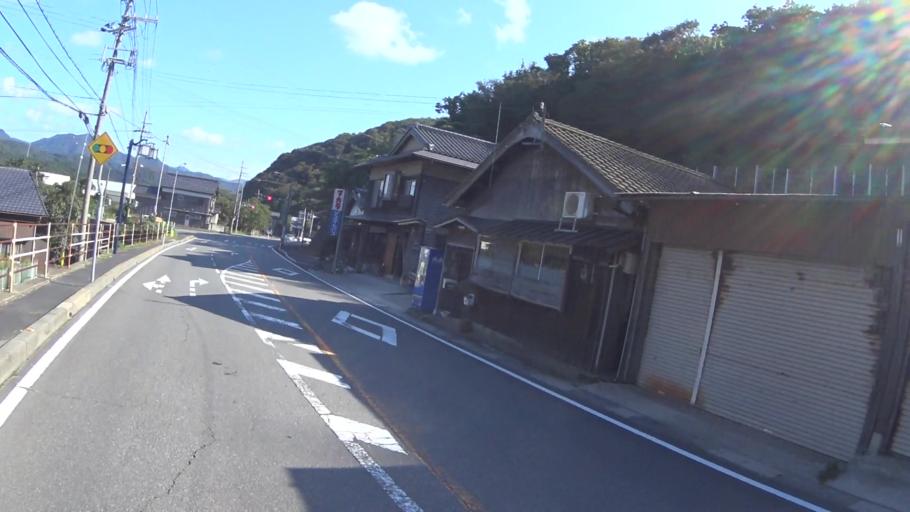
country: JP
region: Kyoto
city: Miyazu
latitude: 35.7316
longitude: 135.0951
